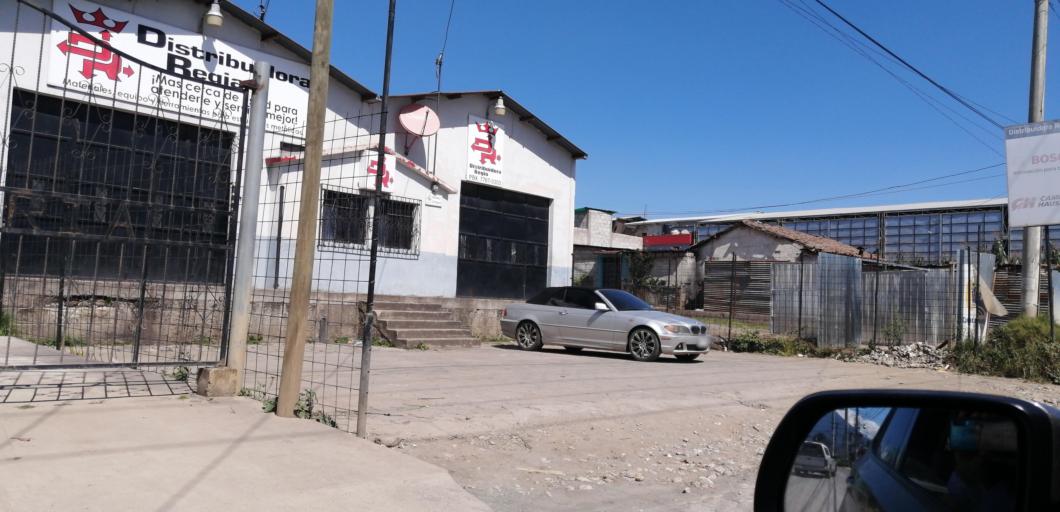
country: GT
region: Quetzaltenango
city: Olintepeque
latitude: 14.8627
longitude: -91.5265
